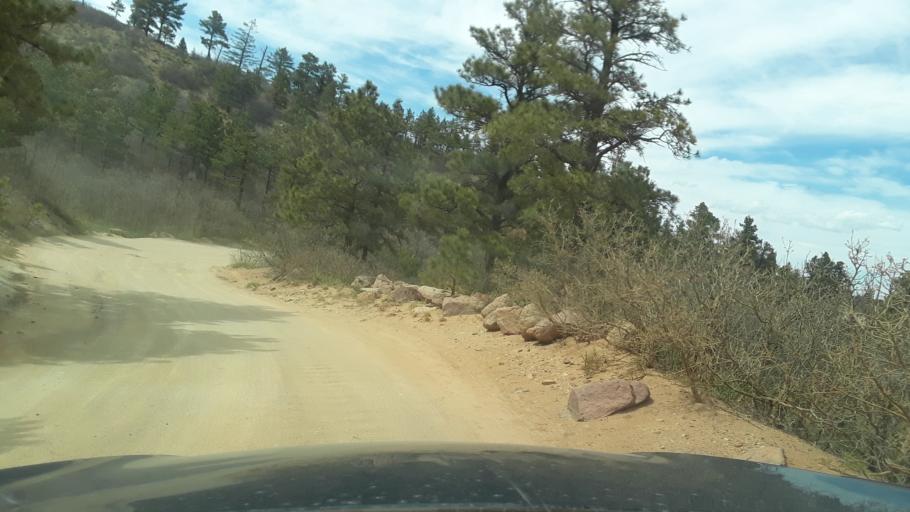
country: US
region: Colorado
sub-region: El Paso County
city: Palmer Lake
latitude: 39.0853
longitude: -104.9117
